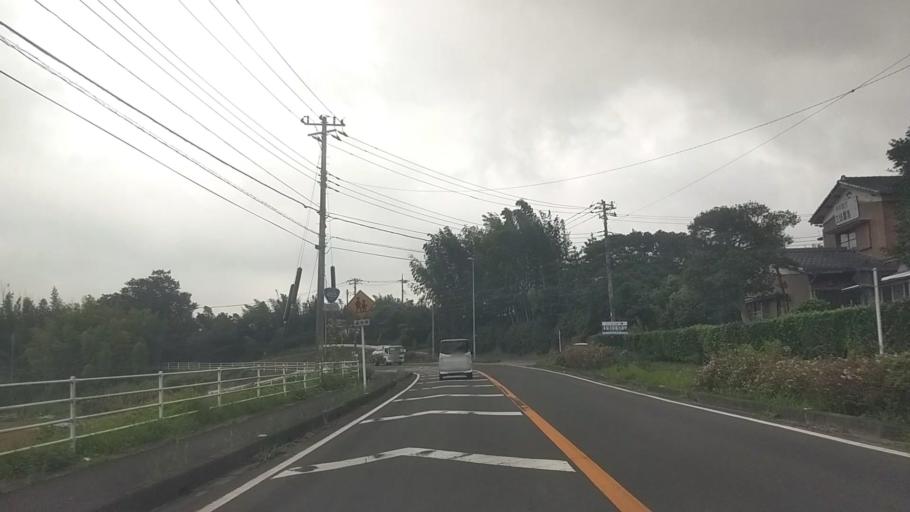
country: JP
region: Chiba
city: Ohara
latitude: 35.2826
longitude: 140.3205
